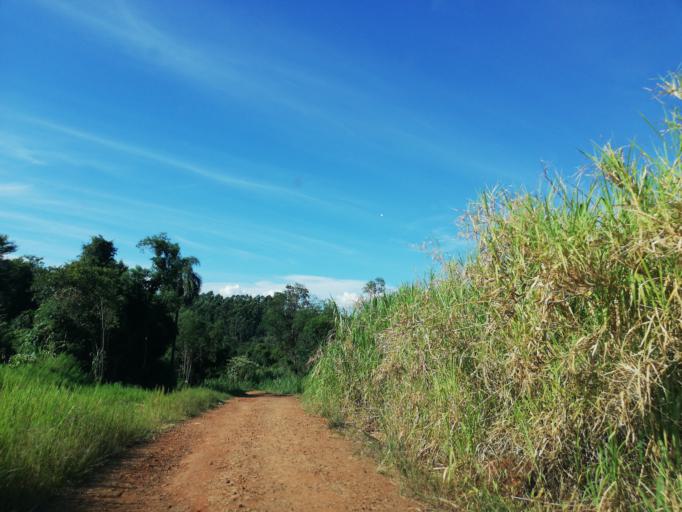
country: AR
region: Misiones
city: Dos de Mayo
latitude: -26.9904
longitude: -54.4957
